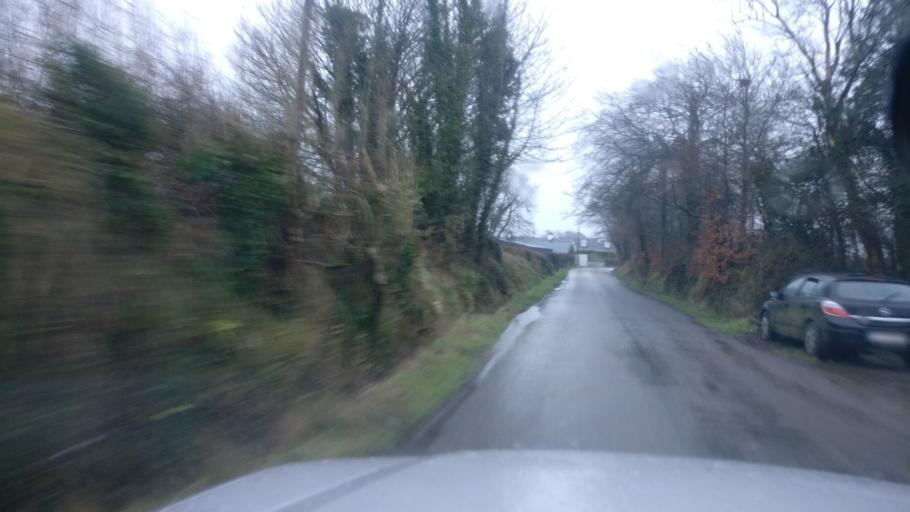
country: IE
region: Connaught
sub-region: County Galway
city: Ballinasloe
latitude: 53.3147
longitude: -8.3687
